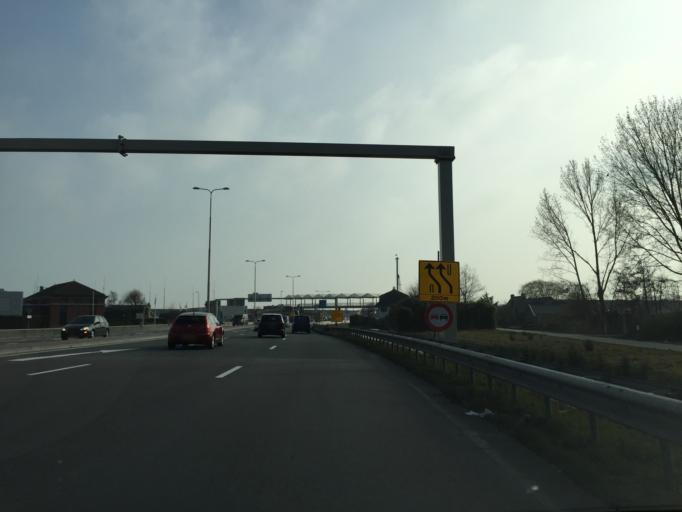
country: NL
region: South Holland
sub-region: Gemeente Westland
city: Naaldwijk
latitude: 51.9802
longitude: 4.2192
